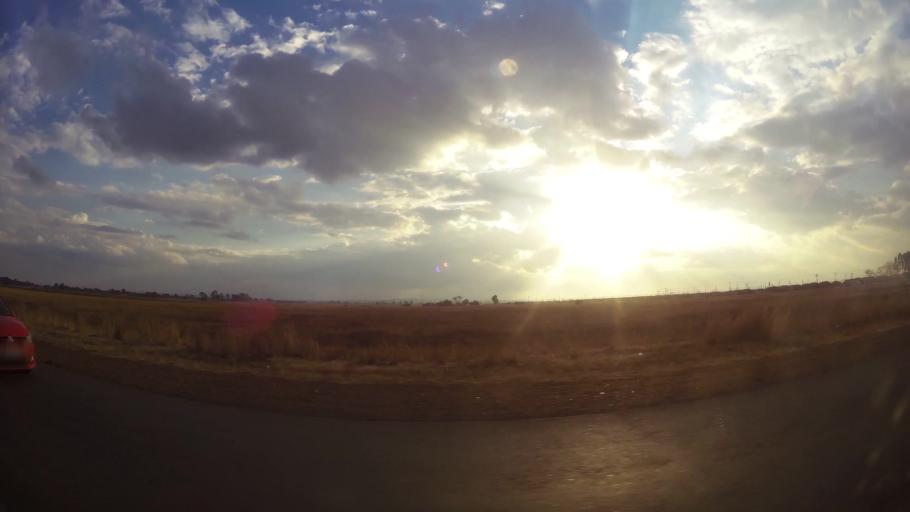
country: ZA
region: Gauteng
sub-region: Sedibeng District Municipality
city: Vanderbijlpark
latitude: -26.6207
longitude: 27.8123
